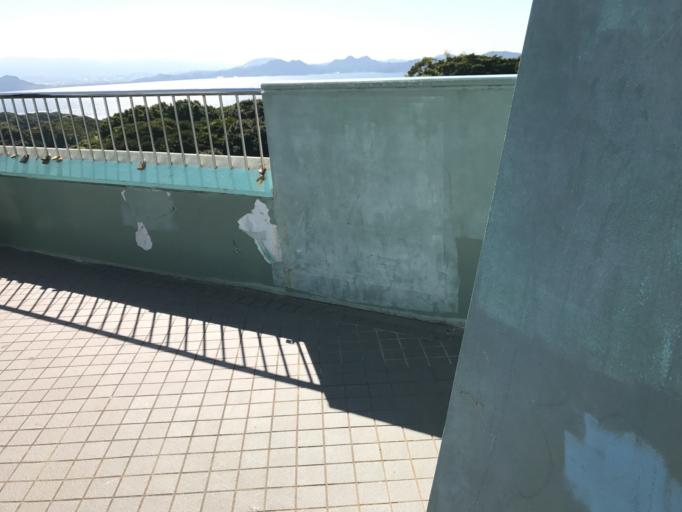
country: JP
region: Fukuoka
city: Fukuoka-shi
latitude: 33.6746
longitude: 130.3072
